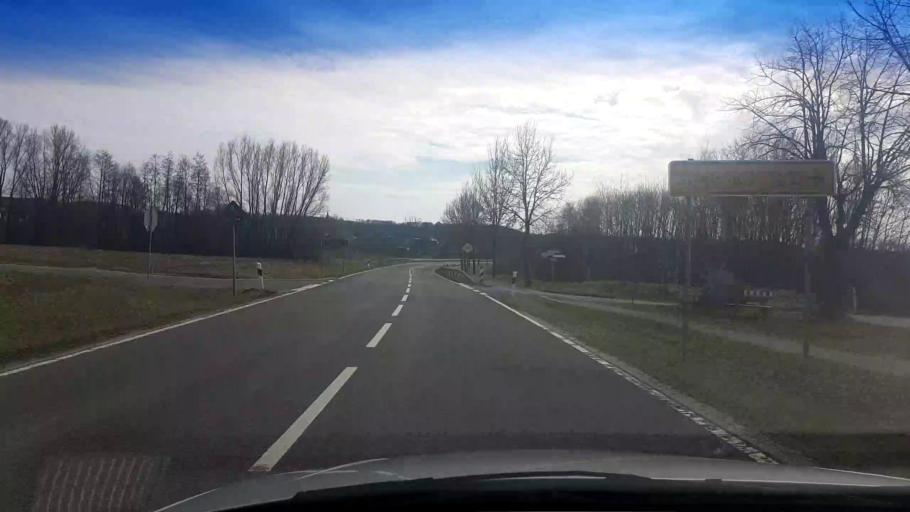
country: DE
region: Bavaria
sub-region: Upper Franconia
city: Frensdorf
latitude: 49.8232
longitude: 10.8653
